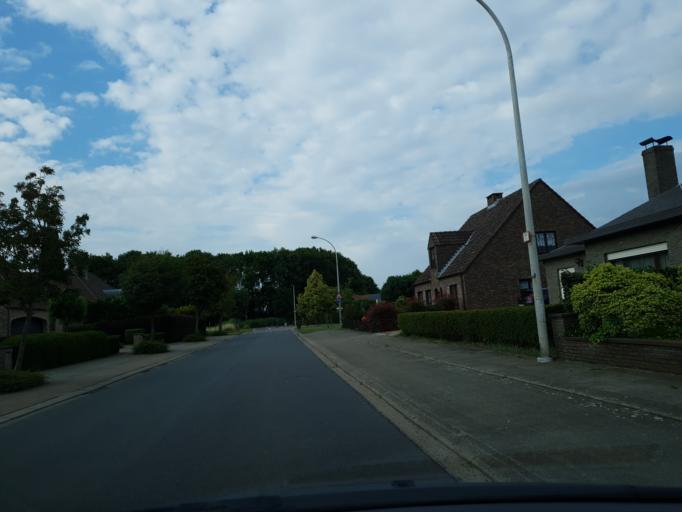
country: BE
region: Flanders
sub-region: Provincie Antwerpen
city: Kapellen
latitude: 51.2701
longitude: 4.4401
